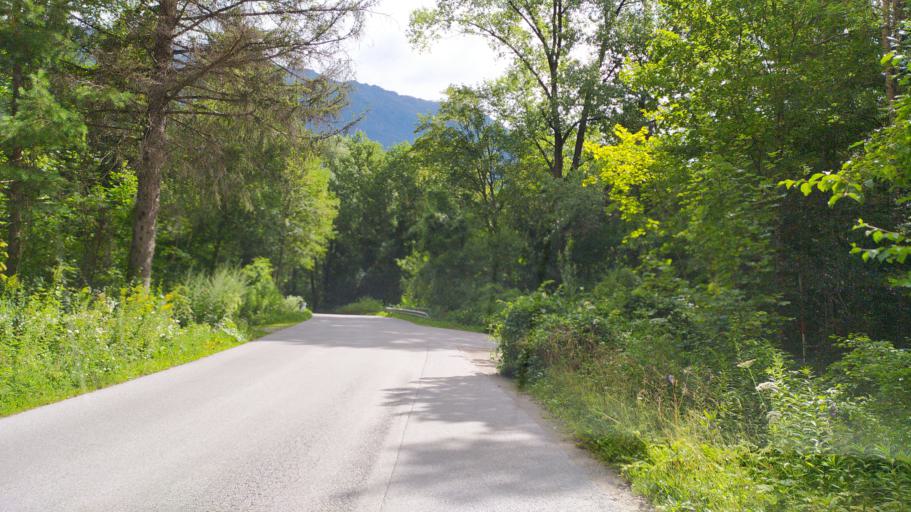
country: AT
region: Tyrol
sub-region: Politischer Bezirk Lienz
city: Lavant
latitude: 46.7891
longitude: 12.8730
